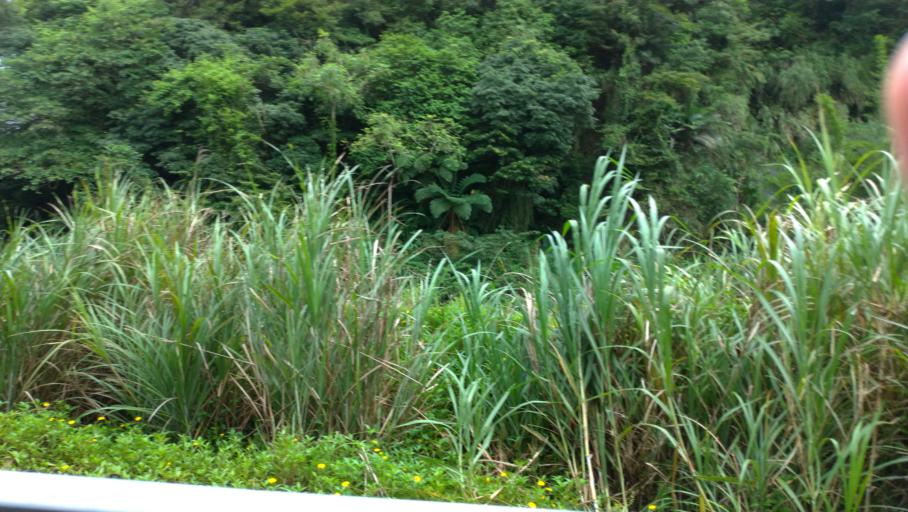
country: TW
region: Taiwan
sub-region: Keelung
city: Keelung
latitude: 25.0483
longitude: 121.7849
